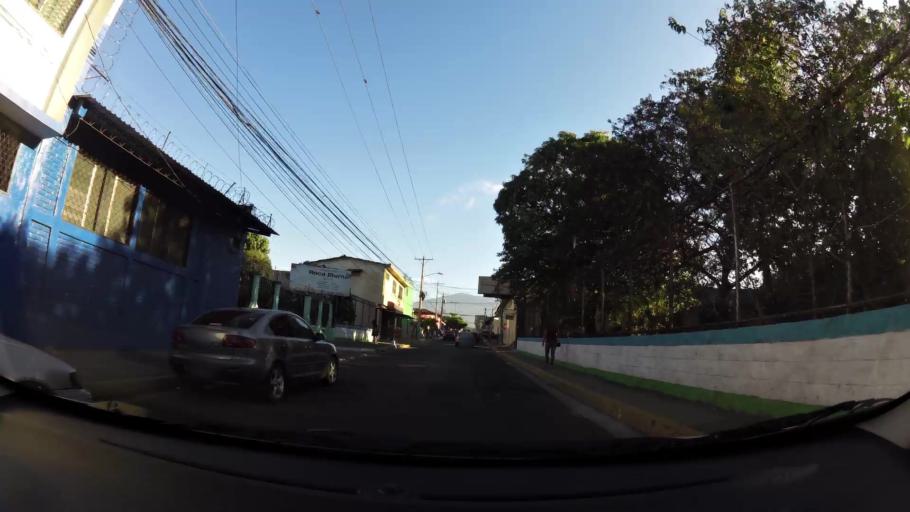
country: SV
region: Sonsonate
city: Sonsonate
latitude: 13.7223
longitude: -89.7254
